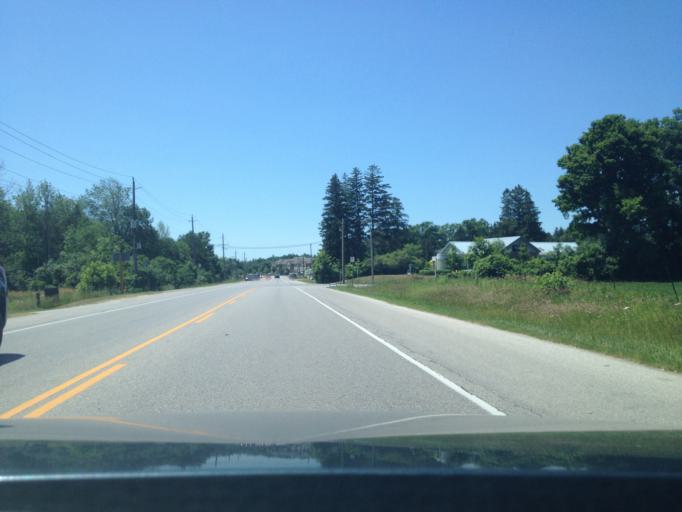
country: CA
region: Ontario
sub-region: Wellington County
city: Guelph
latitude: 43.6919
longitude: -80.4121
